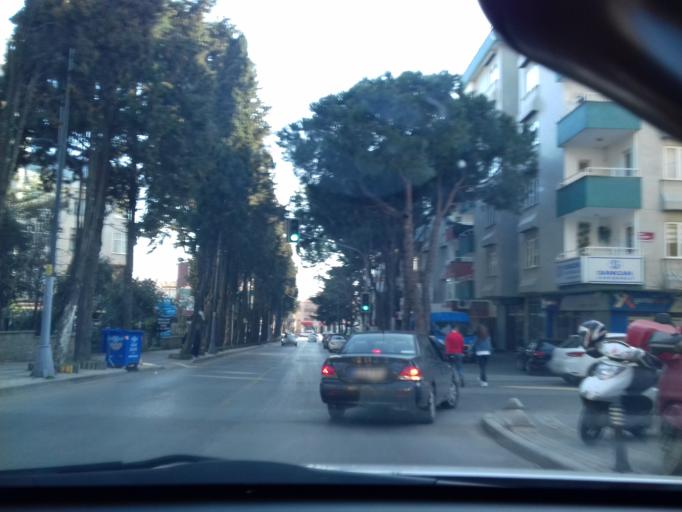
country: TR
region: Istanbul
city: Umraniye
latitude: 41.0207
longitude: 29.0816
